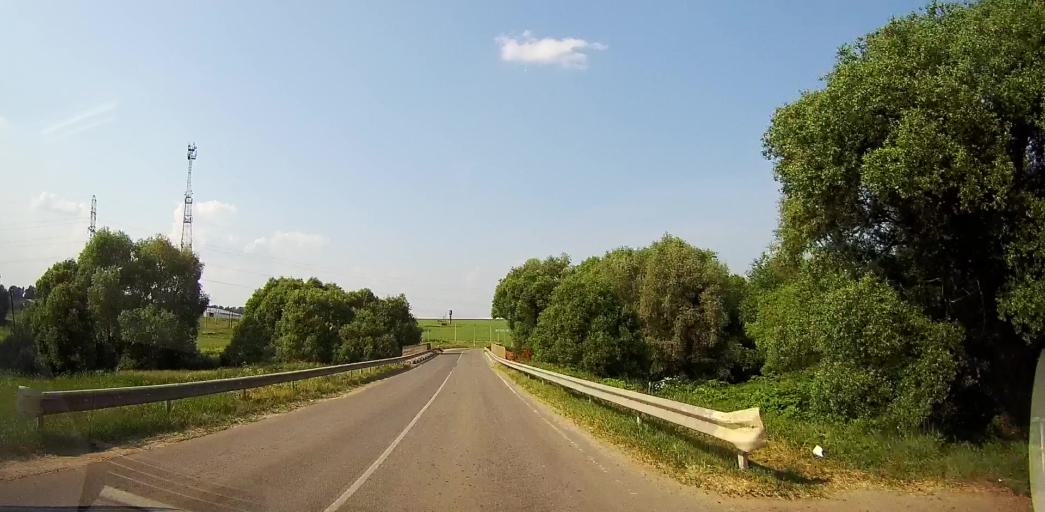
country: RU
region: Moskovskaya
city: Il'inskoye
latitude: 55.2925
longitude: 37.9429
